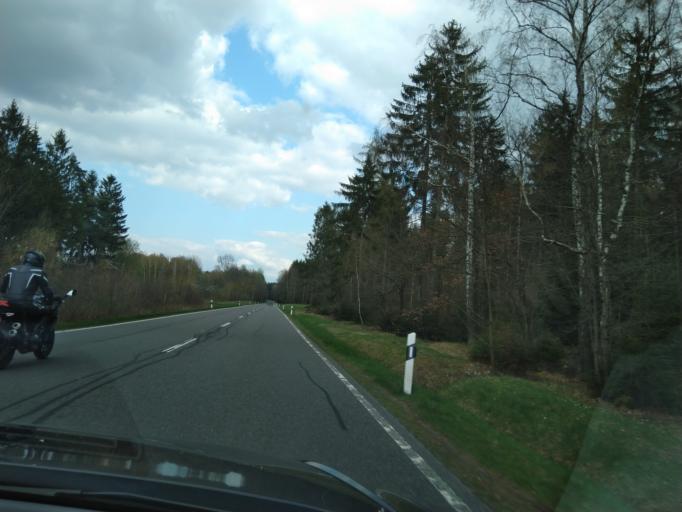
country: DE
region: Saxony
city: Oberschona
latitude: 50.9023
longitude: 13.2955
